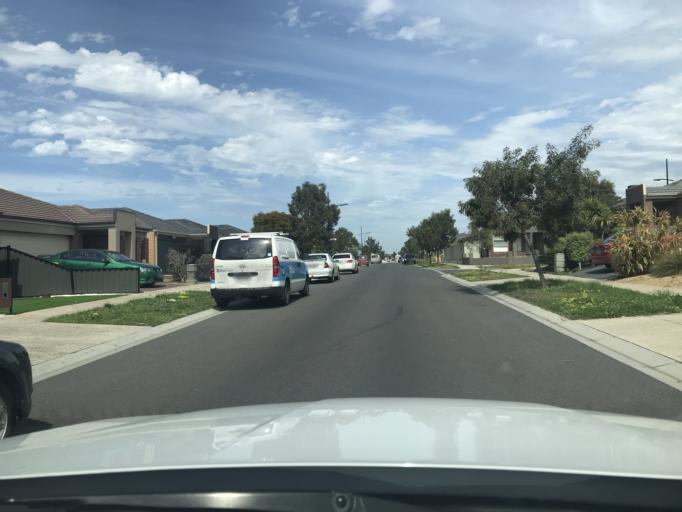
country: AU
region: Victoria
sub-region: Hume
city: Roxburgh Park
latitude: -37.6021
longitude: 144.9120
